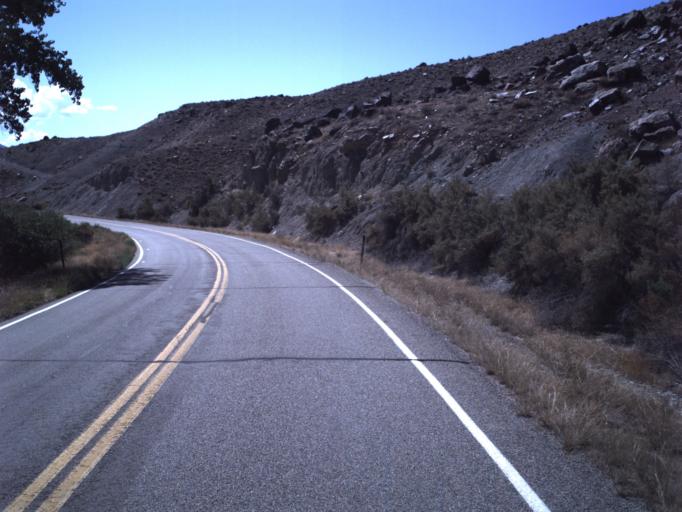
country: US
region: Utah
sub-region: Grand County
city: Moab
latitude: 38.8359
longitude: -109.2877
